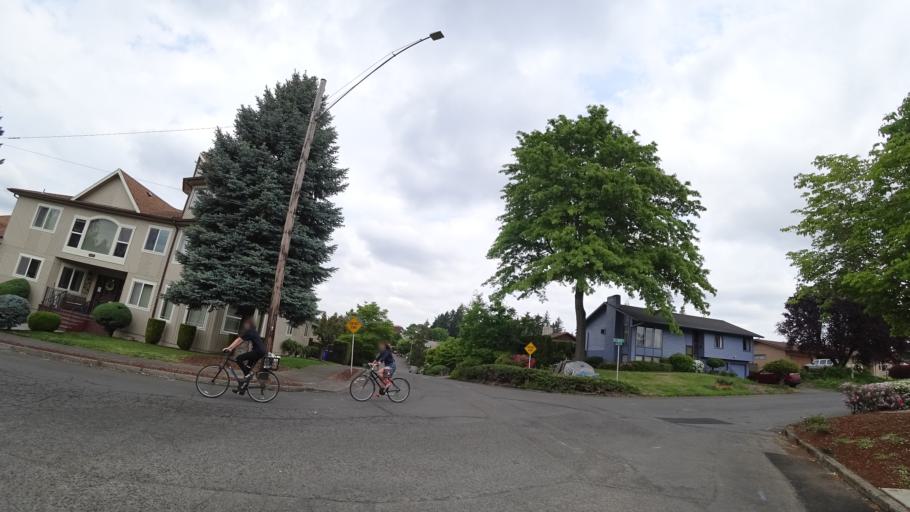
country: US
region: Oregon
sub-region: Clackamas County
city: Milwaukie
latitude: 45.4881
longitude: -122.6325
